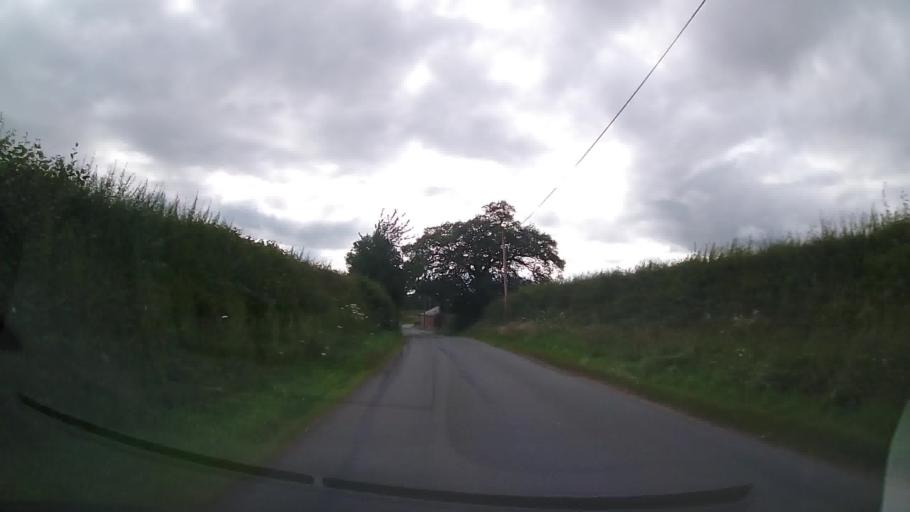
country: GB
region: England
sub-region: Shropshire
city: Wem
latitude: 52.9052
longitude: -2.7263
